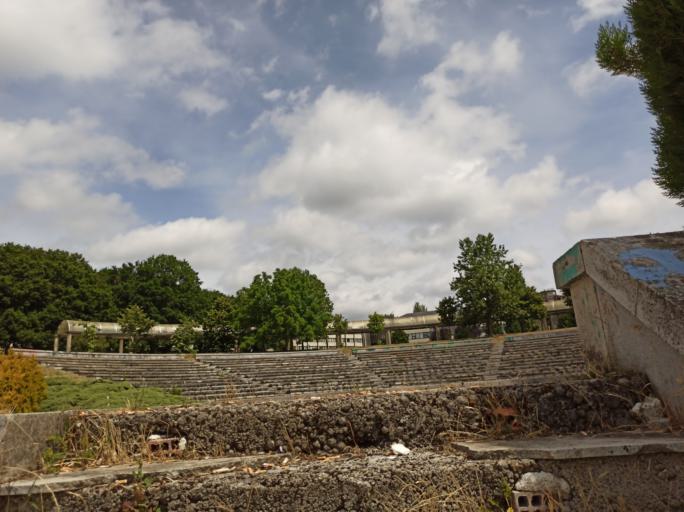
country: ES
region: Galicia
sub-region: Provincia de Lugo
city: Lugo
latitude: 42.9923
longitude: -7.5477
